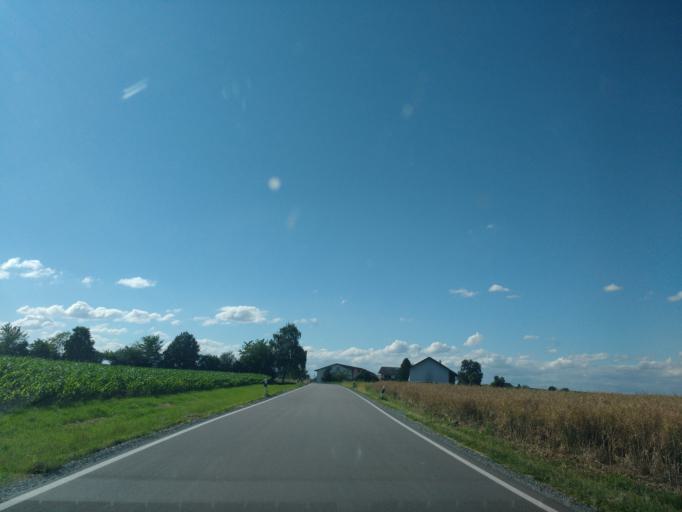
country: DE
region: Bavaria
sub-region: Upper Bavaria
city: Taufkirchen
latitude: 48.1351
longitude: 12.4760
